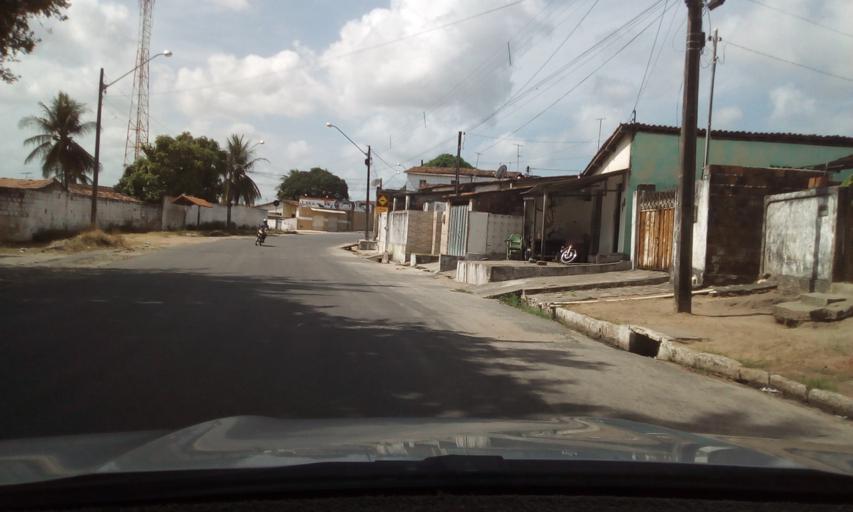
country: BR
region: Paraiba
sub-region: Joao Pessoa
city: Joao Pessoa
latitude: -7.1813
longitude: -34.8838
